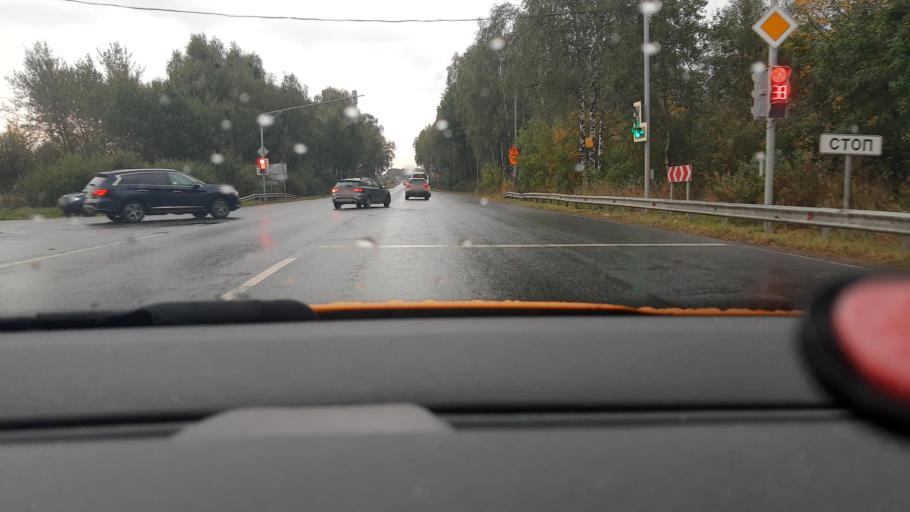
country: RU
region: Moskovskaya
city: Obukhovo
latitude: 55.7995
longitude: 38.2508
